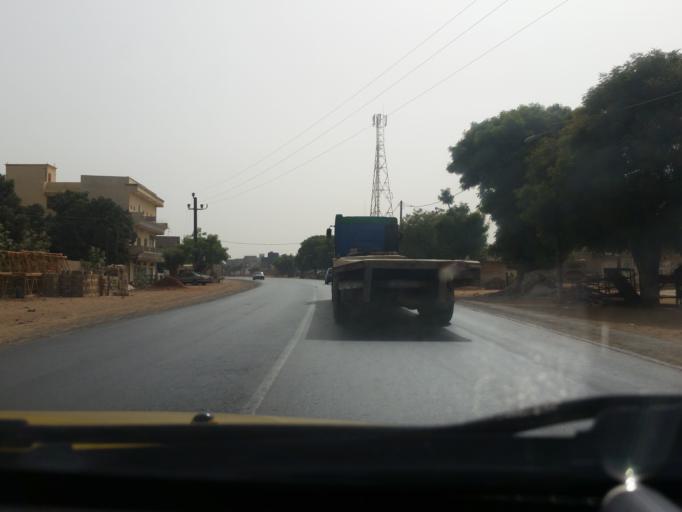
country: SN
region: Thies
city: Pout
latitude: 14.7409
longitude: -17.1392
